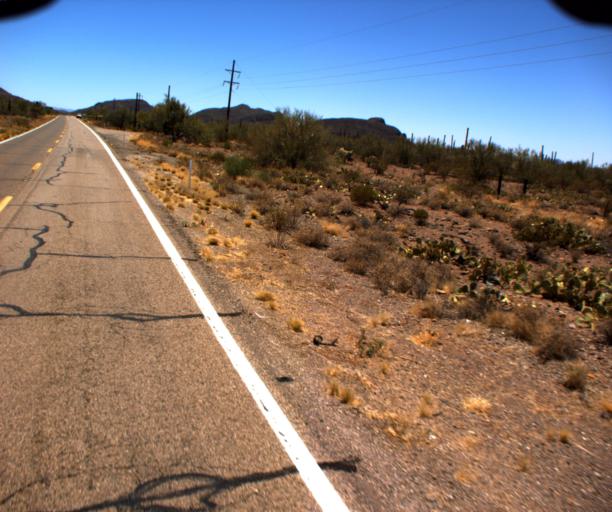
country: US
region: Arizona
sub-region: Pima County
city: Sells
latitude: 31.9842
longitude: -111.9725
